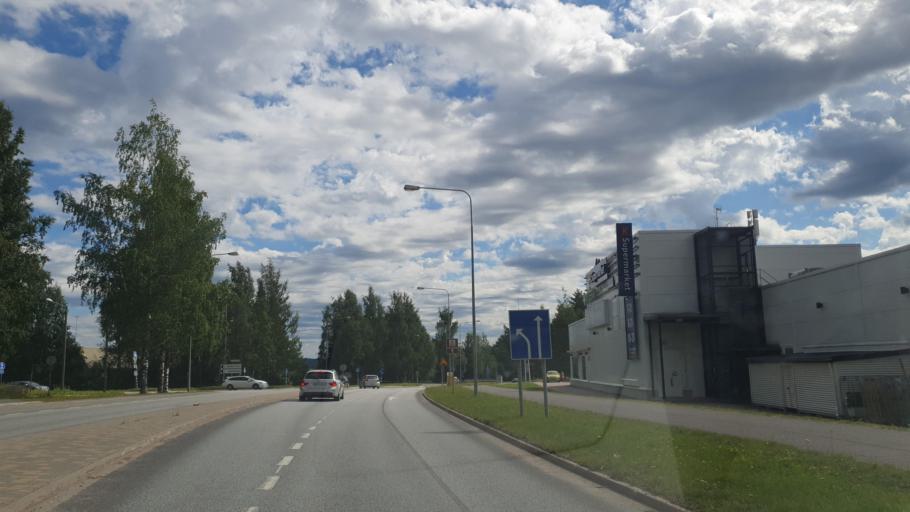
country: FI
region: Central Finland
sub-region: Jyvaeskylae
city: Muurame
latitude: 62.1375
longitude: 25.6736
